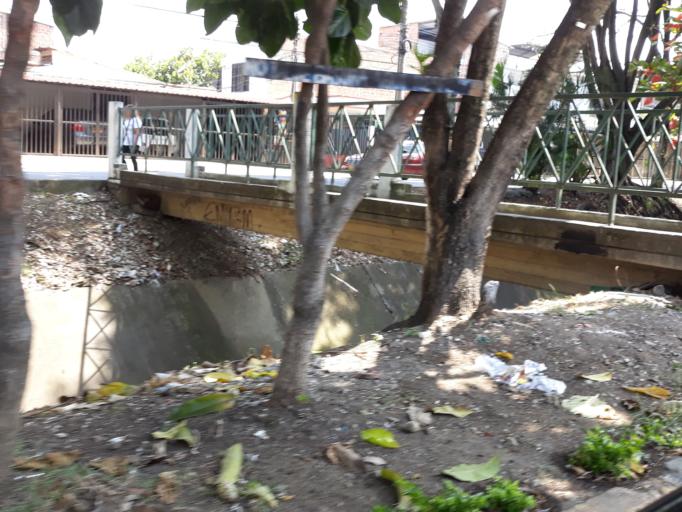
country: CO
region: Valle del Cauca
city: Cali
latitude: 3.4687
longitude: -76.4911
